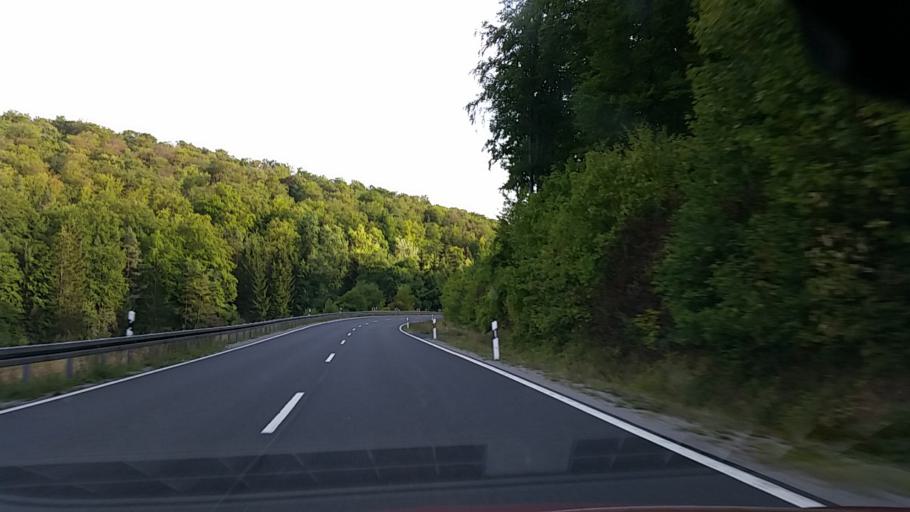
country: DE
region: Thuringia
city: Henneberg
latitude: 50.4760
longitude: 10.3299
